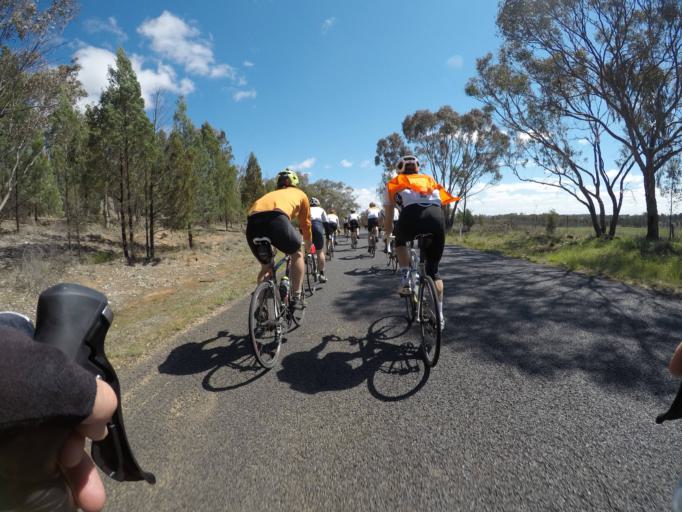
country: AU
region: New South Wales
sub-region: Dubbo Municipality
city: Dubbo
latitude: -32.5852
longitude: 148.5368
